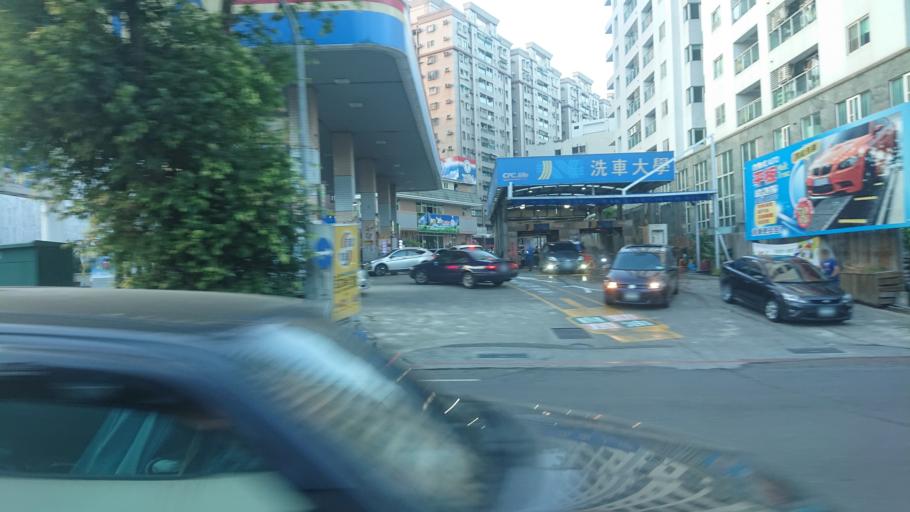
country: TW
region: Taiwan
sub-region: Tainan
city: Tainan
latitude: 23.0099
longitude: 120.2242
